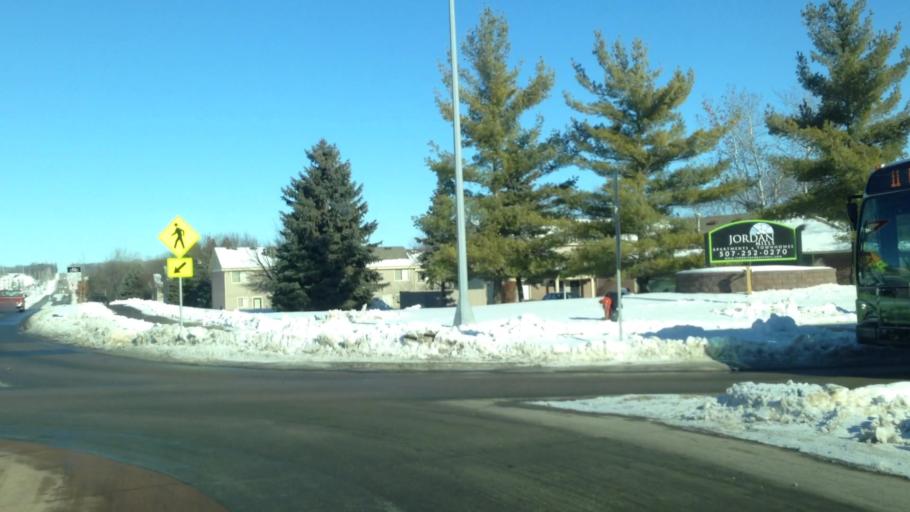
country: US
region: Minnesota
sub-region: Olmsted County
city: Rochester
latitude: 44.0716
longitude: -92.4887
